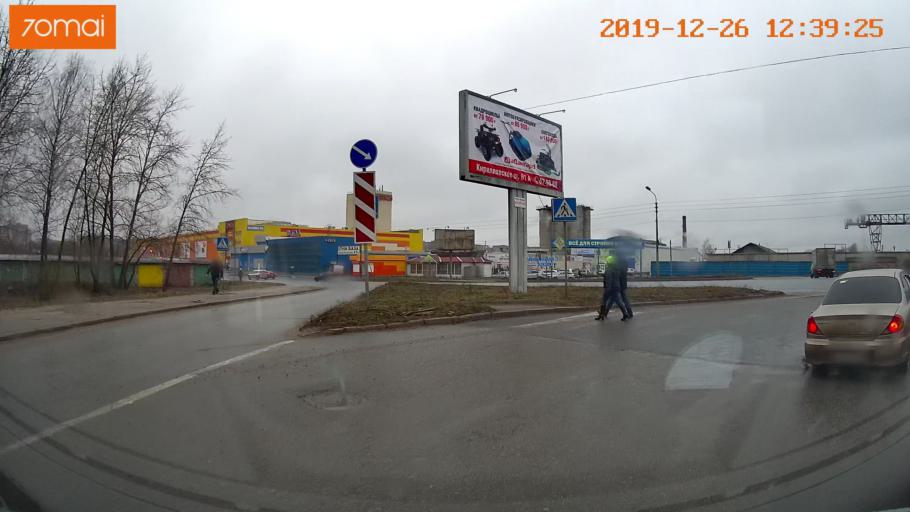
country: RU
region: Vologda
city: Tonshalovo
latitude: 59.1343
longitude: 37.9789
